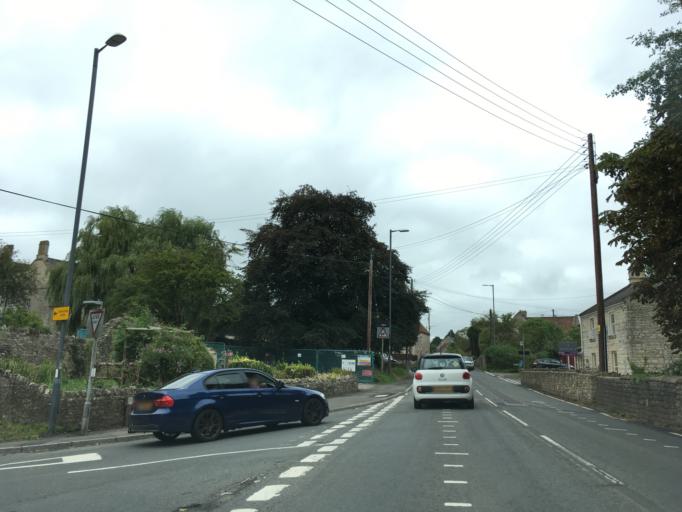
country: GB
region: England
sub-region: Bath and North East Somerset
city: Timsbury
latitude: 51.3434
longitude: -2.4929
